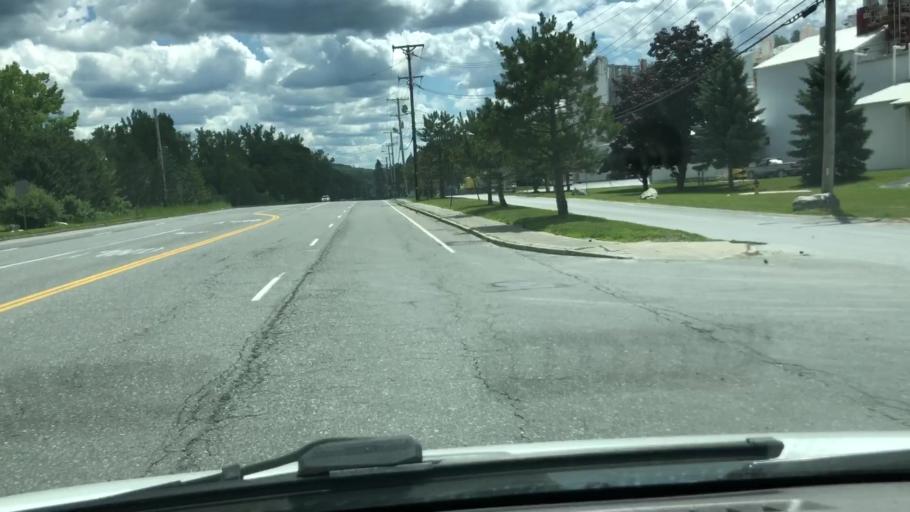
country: US
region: Massachusetts
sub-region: Berkshire County
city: Adams
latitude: 42.6444
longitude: -73.1122
